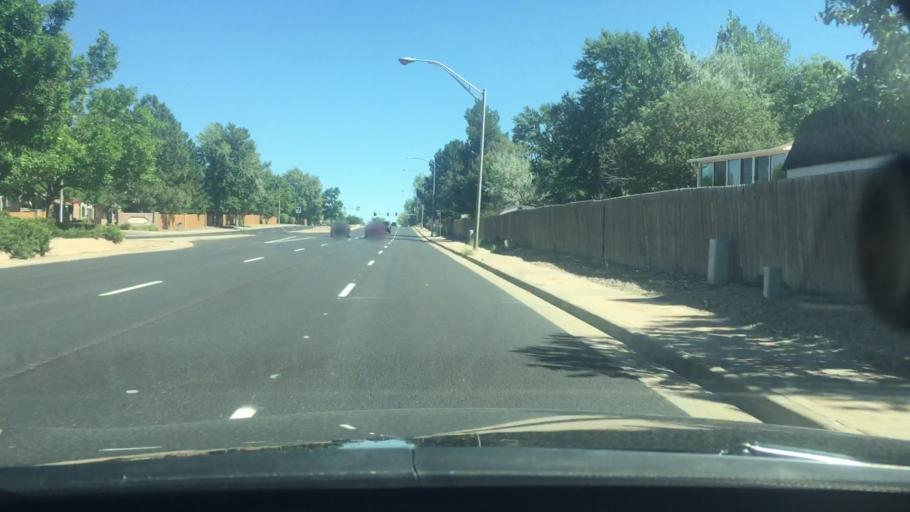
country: US
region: Colorado
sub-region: Arapahoe County
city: Dove Valley
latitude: 39.6384
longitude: -104.8139
